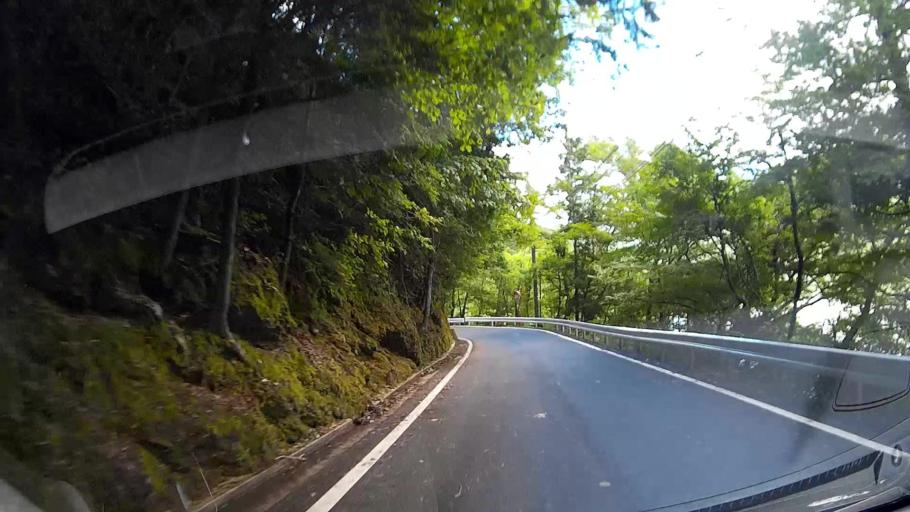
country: JP
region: Shizuoka
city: Shizuoka-shi
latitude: 35.2458
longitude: 138.2432
